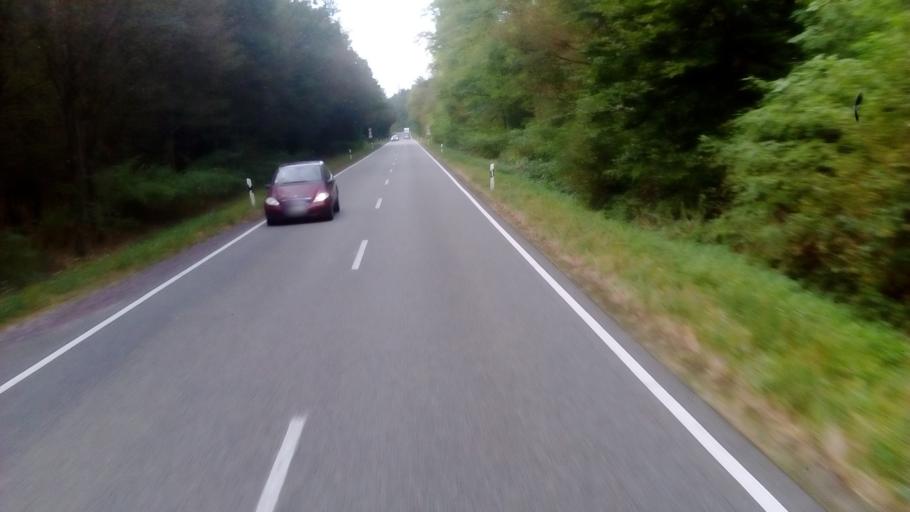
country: DE
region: Rheinland-Pfalz
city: Berg
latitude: 49.0050
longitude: 8.1830
